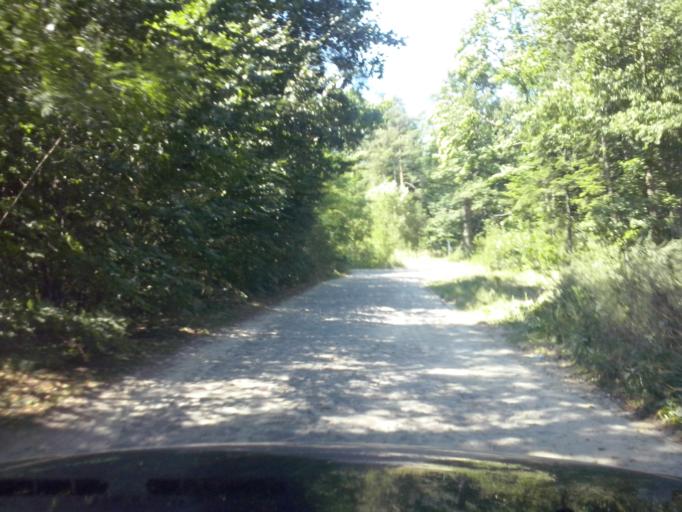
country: PL
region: Swietokrzyskie
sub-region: Powiat kielecki
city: Bieliny
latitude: 50.7808
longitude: 20.9314
